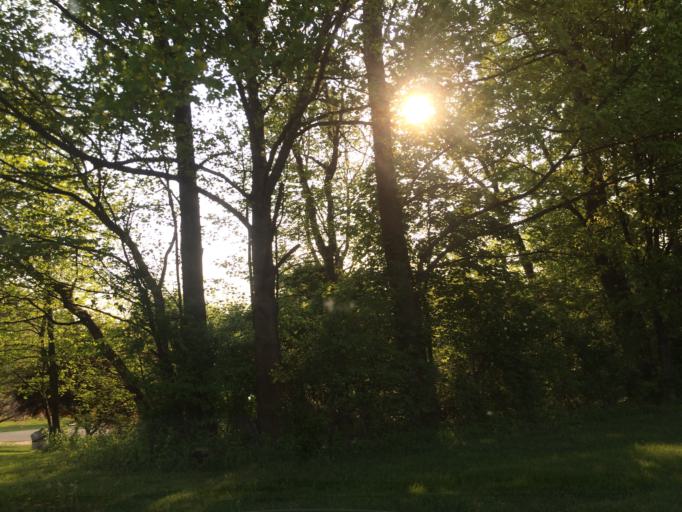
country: US
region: Maryland
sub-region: Carroll County
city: Sykesville
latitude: 39.3960
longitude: -77.0355
